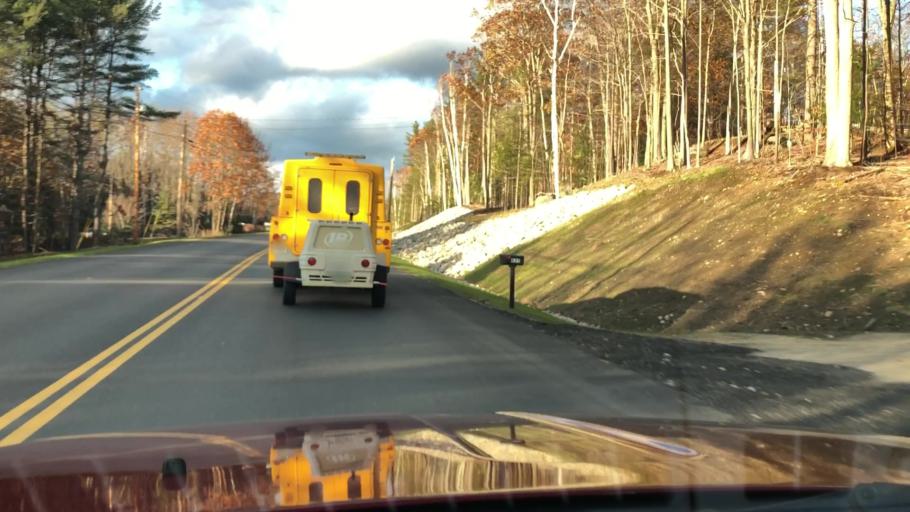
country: US
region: Maine
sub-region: Oxford County
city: Peru
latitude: 44.5202
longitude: -70.4081
